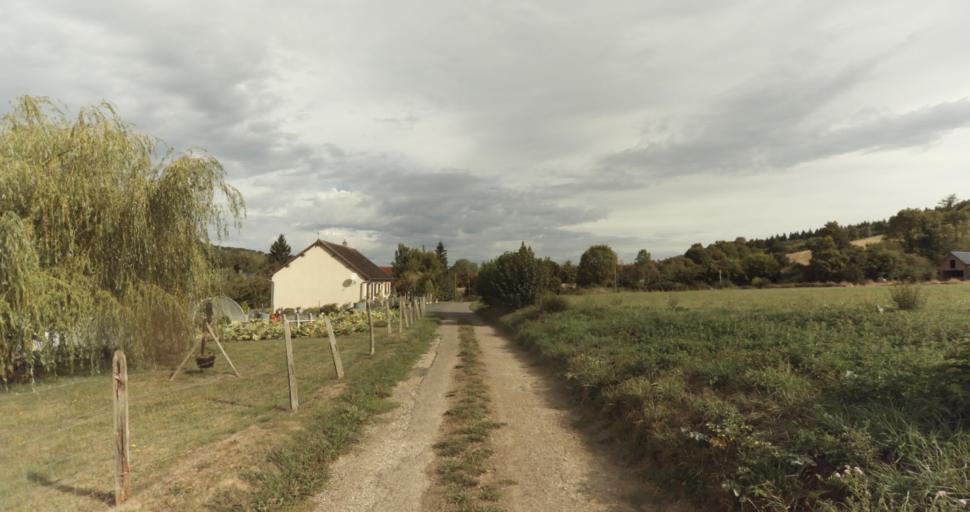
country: FR
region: Lower Normandy
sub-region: Departement de l'Orne
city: Vimoutiers
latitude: 48.9282
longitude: 0.2719
